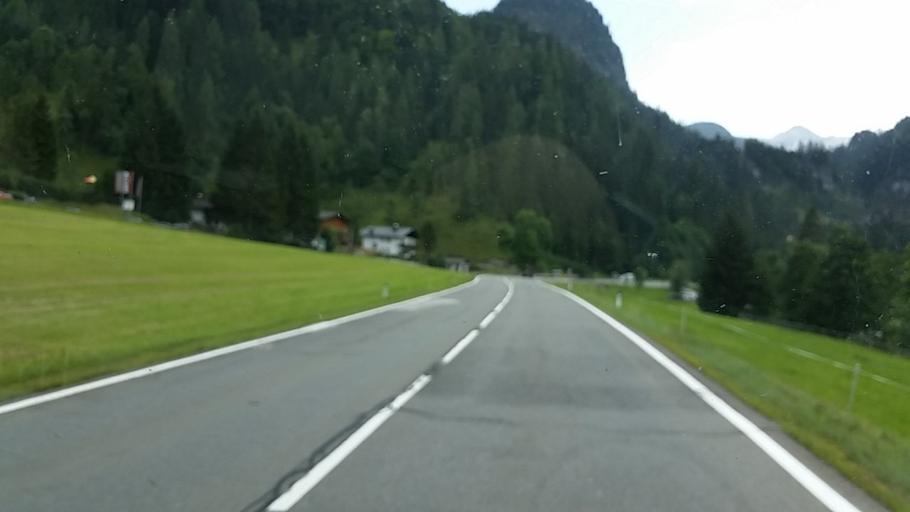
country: AT
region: Salzburg
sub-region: Politischer Bezirk Sankt Johann im Pongau
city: Untertauern
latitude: 47.3028
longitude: 13.5059
